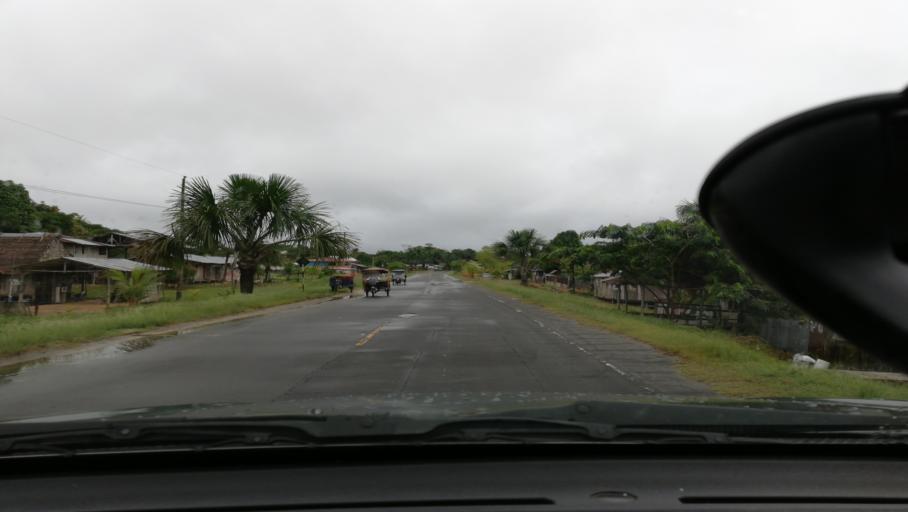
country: PE
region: Loreto
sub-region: Provincia de Loreto
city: Nauta
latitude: -4.2208
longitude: -73.4827
